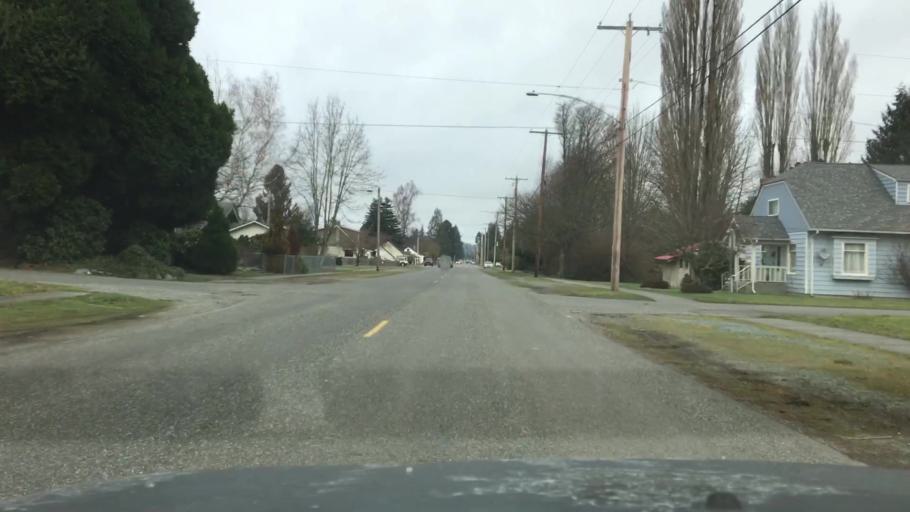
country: US
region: Washington
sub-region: Skagit County
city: Sedro-Woolley
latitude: 48.4950
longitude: -122.2260
